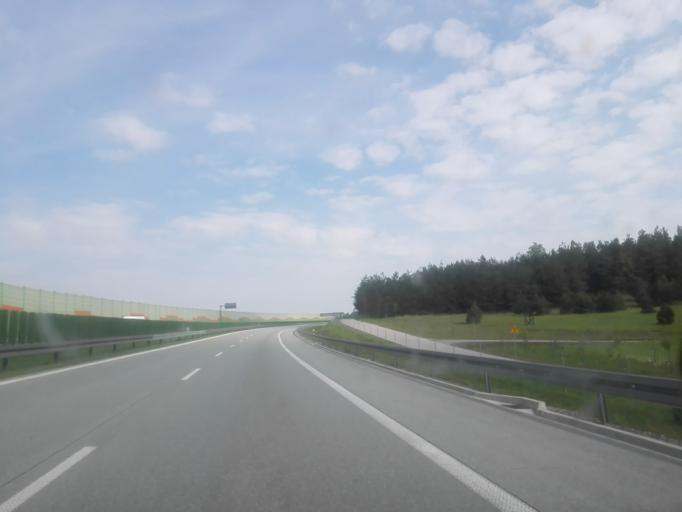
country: PL
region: Lodz Voivodeship
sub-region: Powiat rawski
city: Rawa Mazowiecka
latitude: 51.7104
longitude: 20.2191
